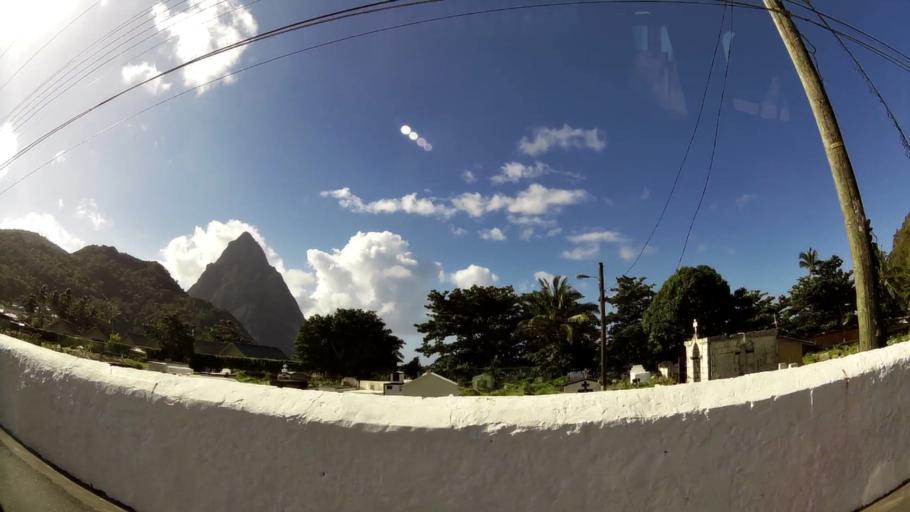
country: LC
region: Soufriere
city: Soufriere
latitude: 13.8574
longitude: -61.0610
